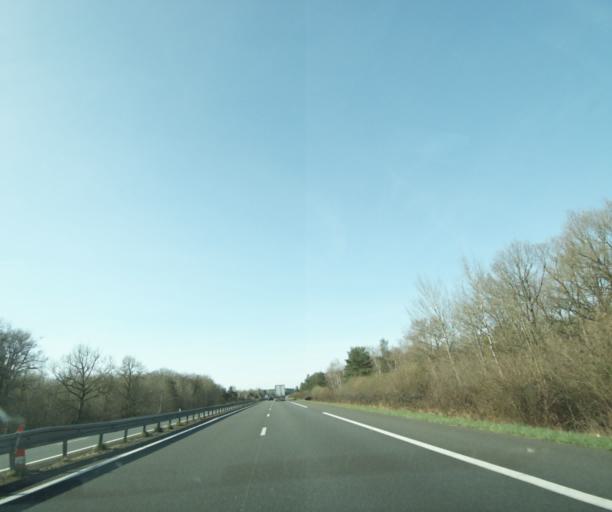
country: FR
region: Centre
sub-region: Departement du Loiret
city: Jouy-le-Potier
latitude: 47.7415
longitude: 1.8678
